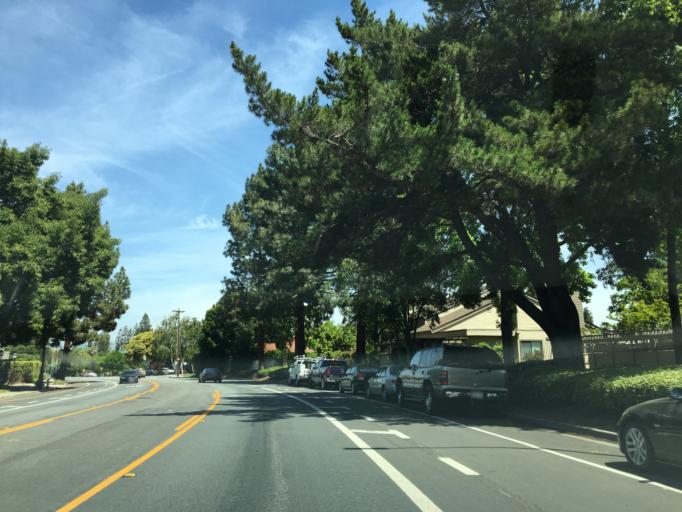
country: US
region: California
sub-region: Santa Clara County
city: Buena Vista
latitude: 37.2929
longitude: -121.9064
